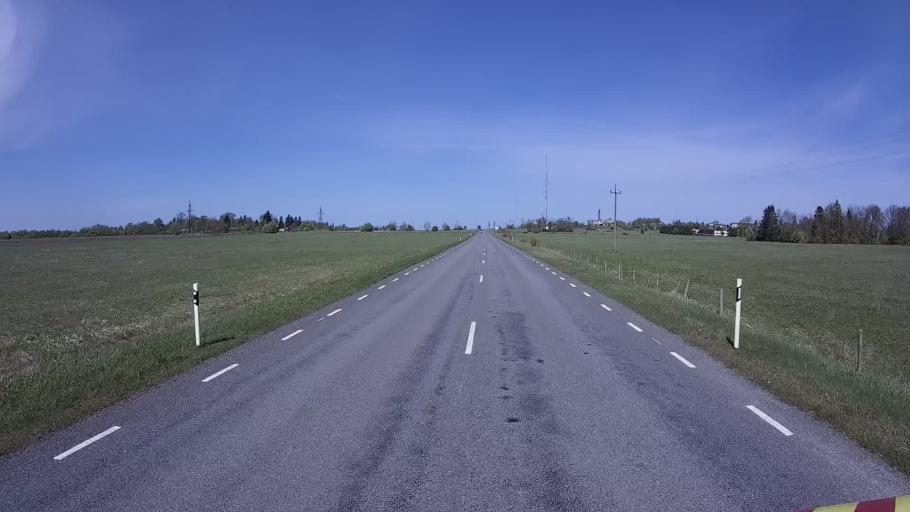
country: EE
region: Laeaene
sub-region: Lihula vald
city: Lihula
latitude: 58.6690
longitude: 23.8305
